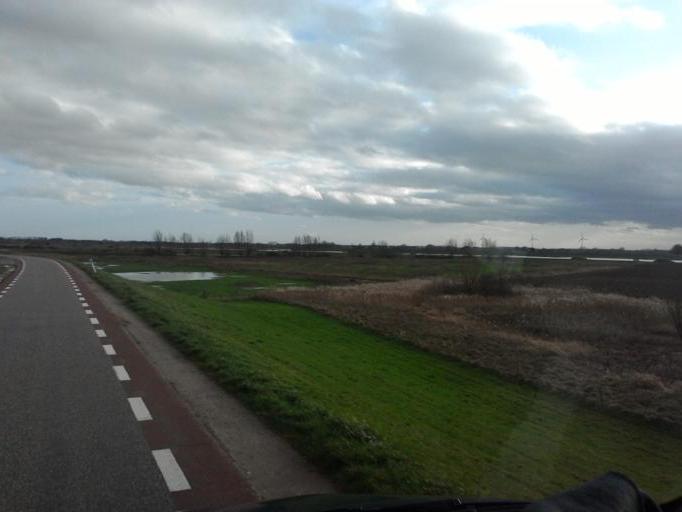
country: NL
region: Gelderland
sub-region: Gemeente Culemborg
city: Culemborg
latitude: 51.9668
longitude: 5.1947
